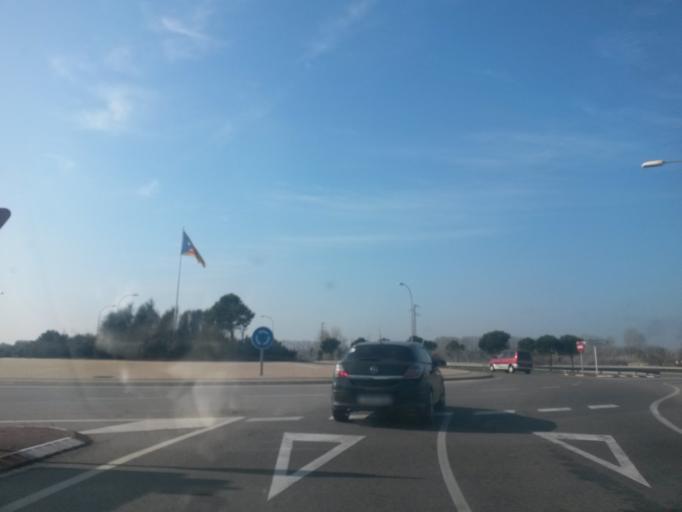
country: ES
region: Catalonia
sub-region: Provincia de Girona
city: Castello d'Empuries
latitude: 42.2606
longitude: 3.0943
